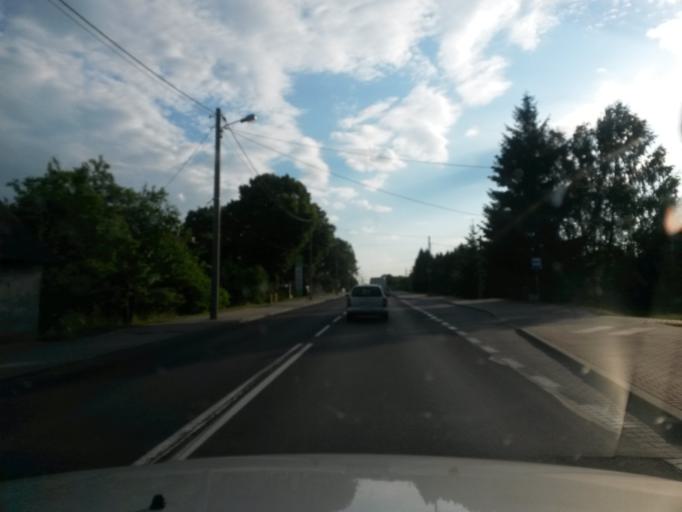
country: PL
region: Lodz Voivodeship
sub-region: Powiat belchatowski
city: Belchatow
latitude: 51.3575
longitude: 19.3447
